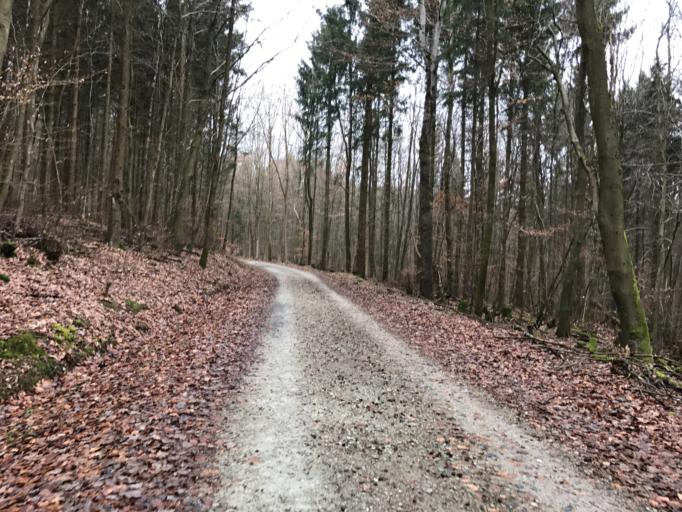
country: DE
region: Hesse
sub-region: Regierungsbezirk Darmstadt
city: Niedernhausen
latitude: 50.1535
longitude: 8.2942
